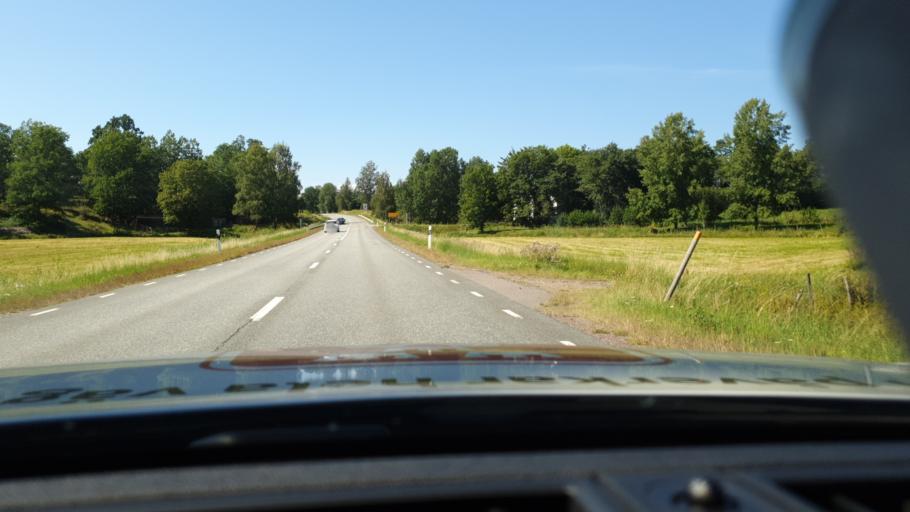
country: SE
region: Joenkoeping
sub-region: Jonkopings Kommun
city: Asa
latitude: 58.0065
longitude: 14.5902
